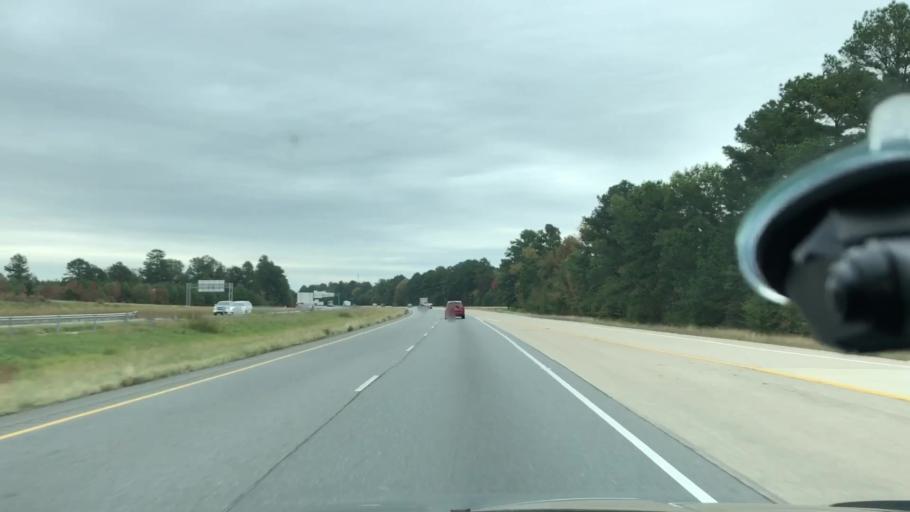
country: US
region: Arkansas
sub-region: Miller County
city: Texarkana
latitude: 33.4804
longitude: -93.9852
